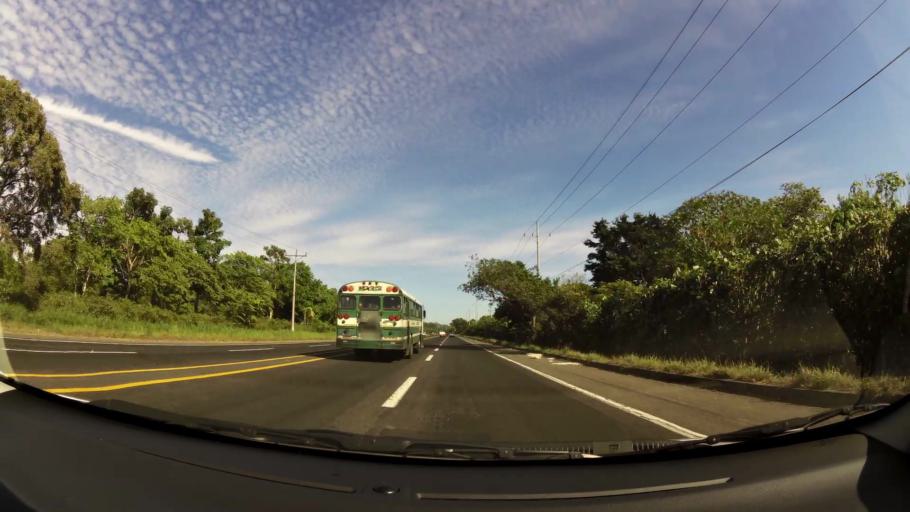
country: SV
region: Santa Ana
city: Santa Ana
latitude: 13.9884
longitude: -89.6174
